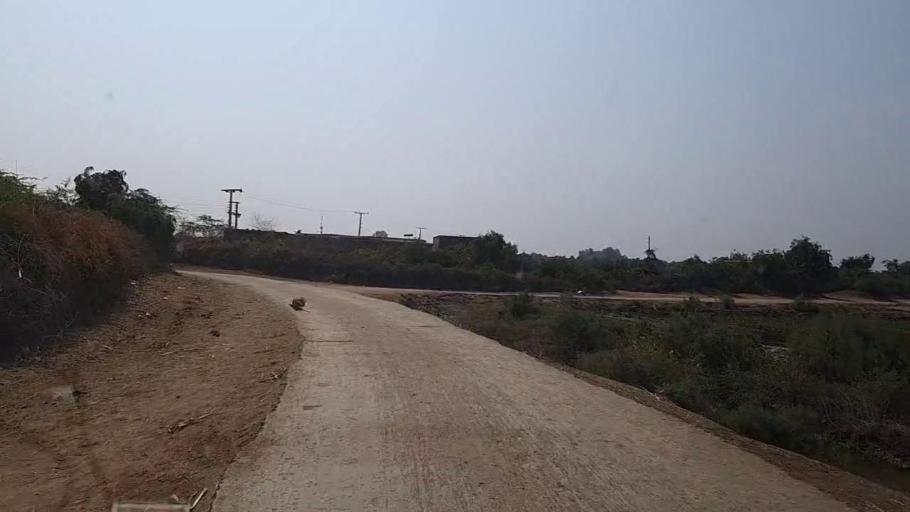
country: PK
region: Sindh
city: Mirwah Gorchani
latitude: 25.3245
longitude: 69.0169
